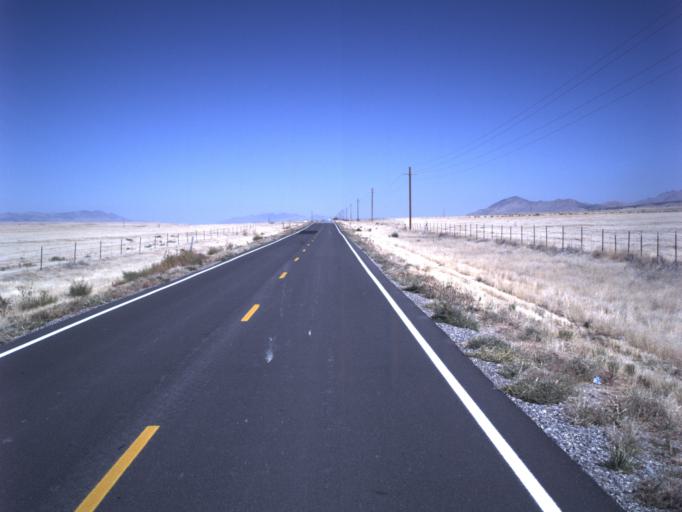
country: US
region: Utah
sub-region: Tooele County
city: Grantsville
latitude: 40.3931
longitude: -112.7475
